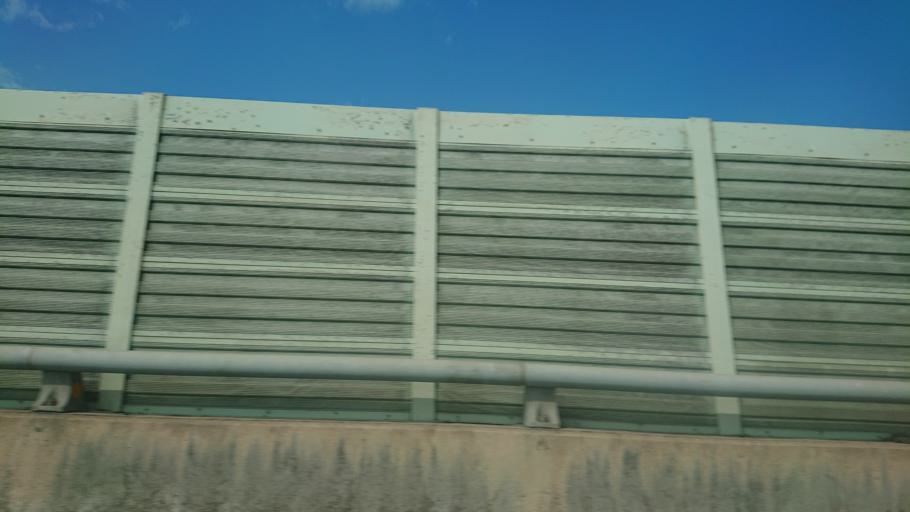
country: TW
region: Taiwan
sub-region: Changhua
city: Chang-hua
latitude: 24.0676
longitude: 120.4127
